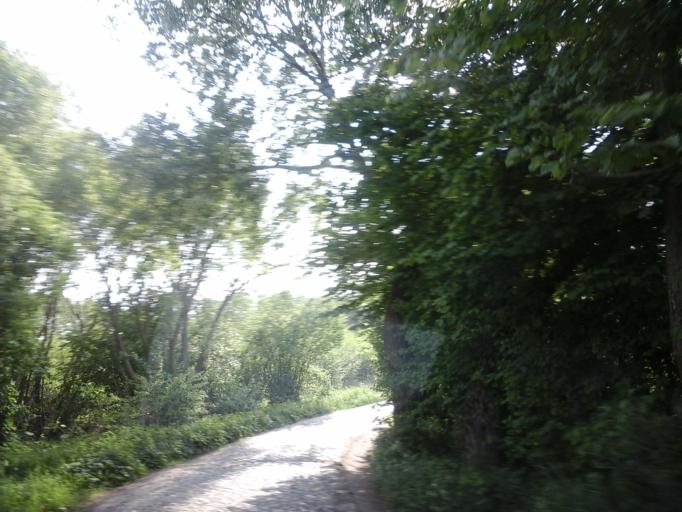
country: PL
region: West Pomeranian Voivodeship
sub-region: Powiat mysliborski
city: Barlinek
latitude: 53.0451
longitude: 15.2083
